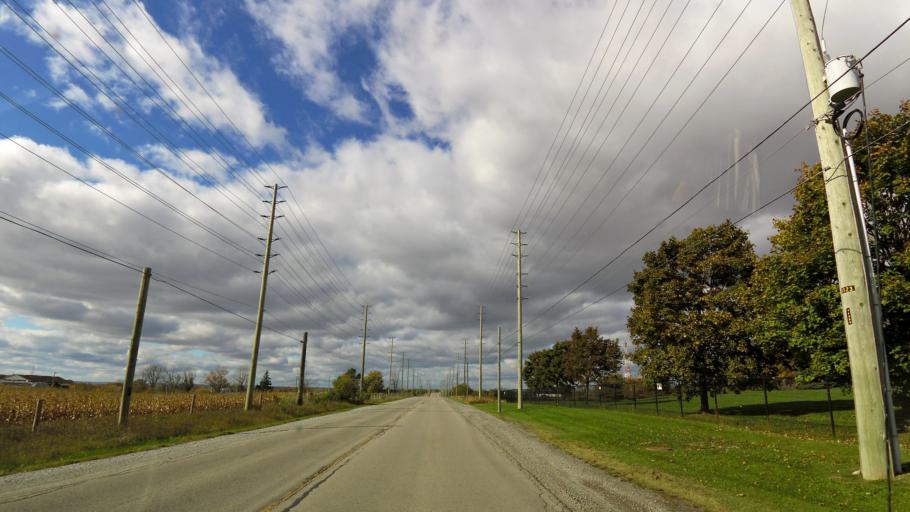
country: CA
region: Ontario
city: Oakville
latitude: 43.4959
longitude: -79.7516
